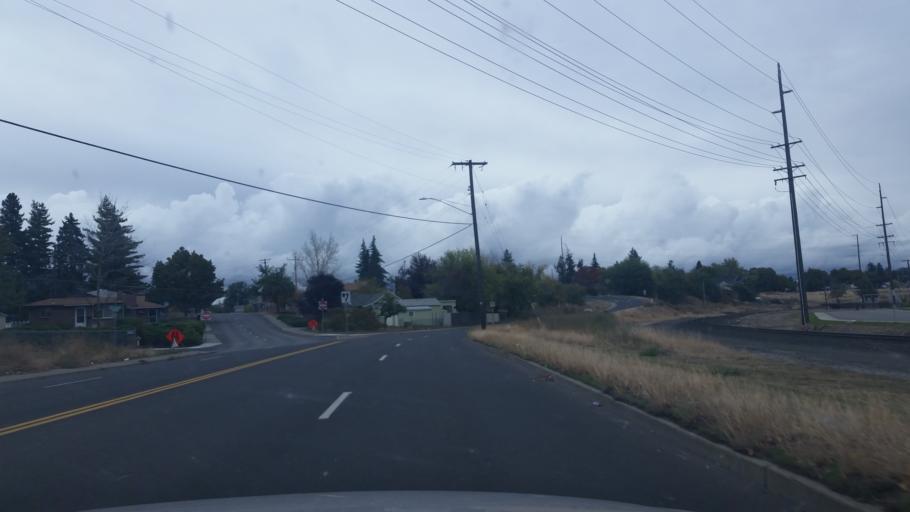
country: US
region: Washington
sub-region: Spokane County
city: Spokane
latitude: 47.6761
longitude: -117.3900
